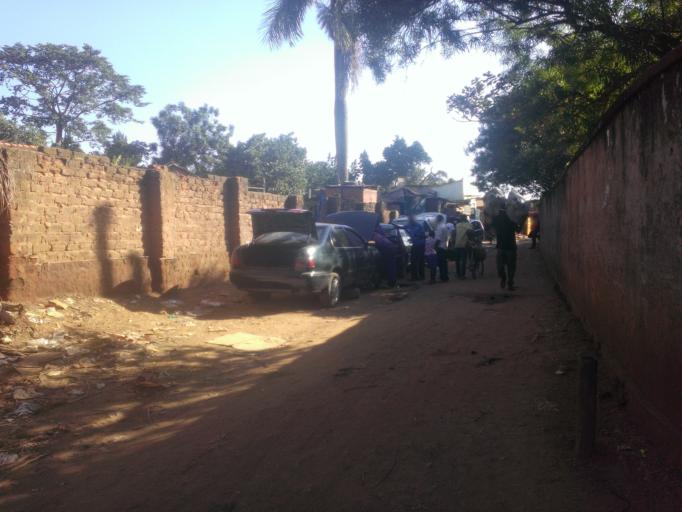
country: UG
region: Central Region
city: Kampala Central Division
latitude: 0.3262
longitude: 32.5605
